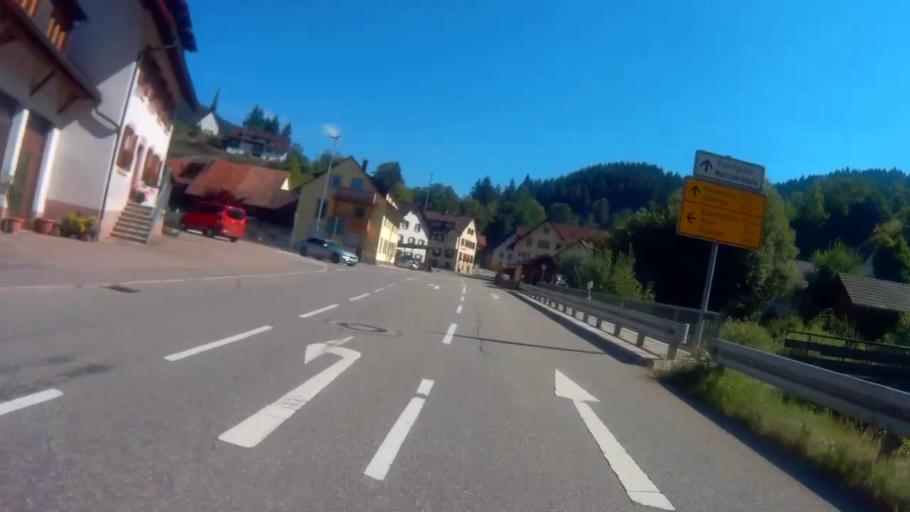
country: DE
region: Baden-Wuerttemberg
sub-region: Freiburg Region
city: Hausen
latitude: 47.7188
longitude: 7.7950
